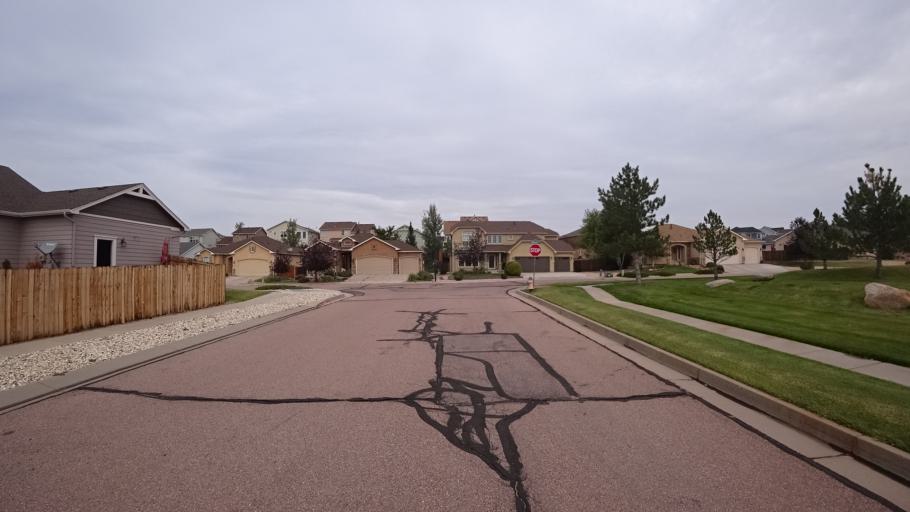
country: US
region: Colorado
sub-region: El Paso County
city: Cimarron Hills
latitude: 38.9138
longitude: -104.6878
